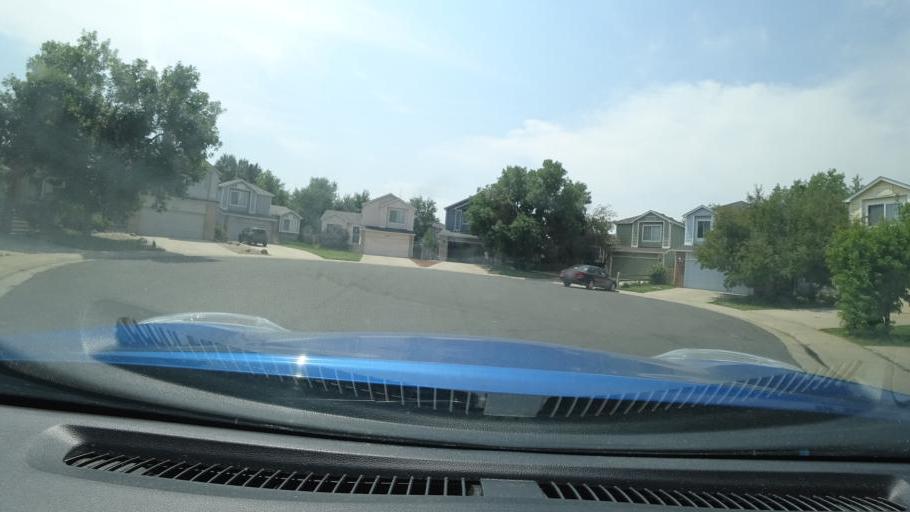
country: US
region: Colorado
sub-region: Adams County
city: Aurora
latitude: 39.7718
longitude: -104.7612
